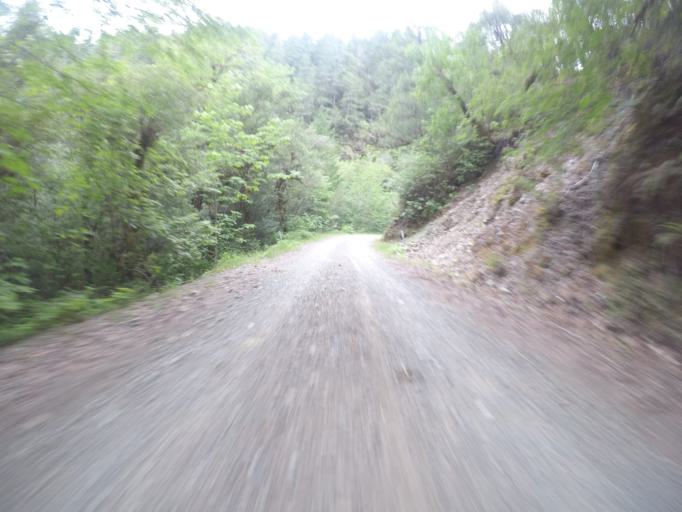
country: US
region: California
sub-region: Del Norte County
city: Bertsch-Oceanview
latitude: 41.7336
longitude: -123.8822
